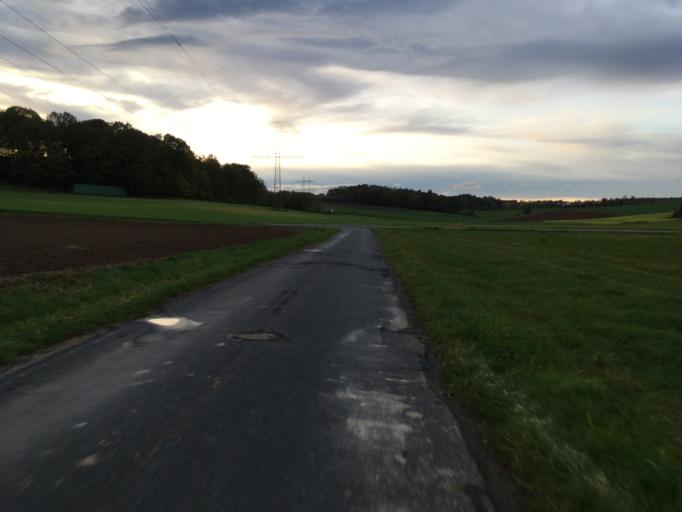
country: DE
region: Baden-Wuerttemberg
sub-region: Karlsruhe Region
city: Rosenberg
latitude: 49.3912
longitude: 9.4936
